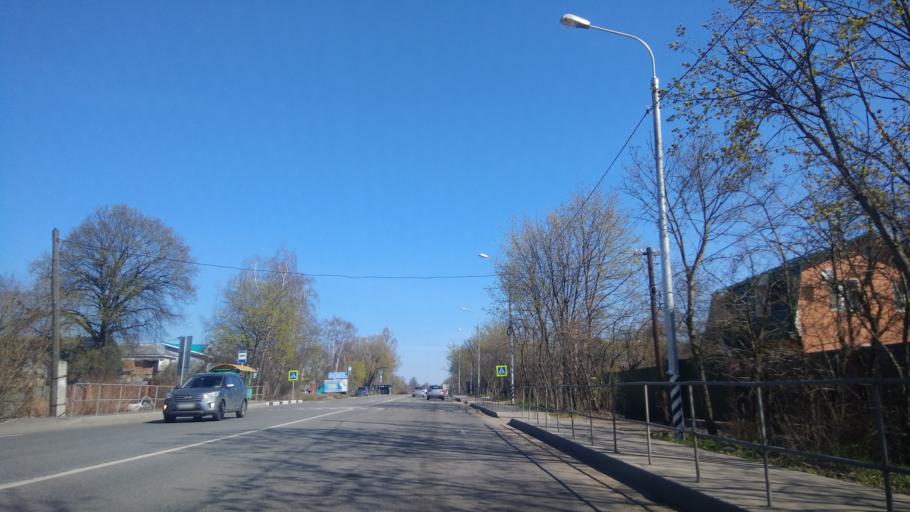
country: RU
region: Moskovskaya
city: Pushkino
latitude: 56.0147
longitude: 37.8720
